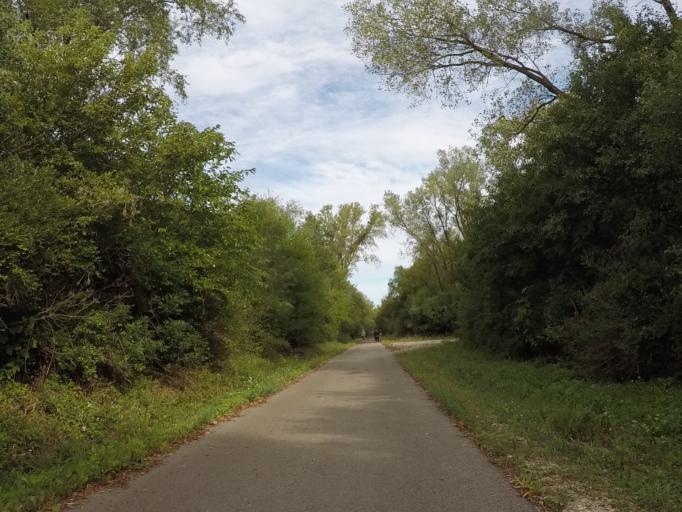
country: US
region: Wisconsin
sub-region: Sauk County
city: Prairie du Sac
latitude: 43.3266
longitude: -89.7472
